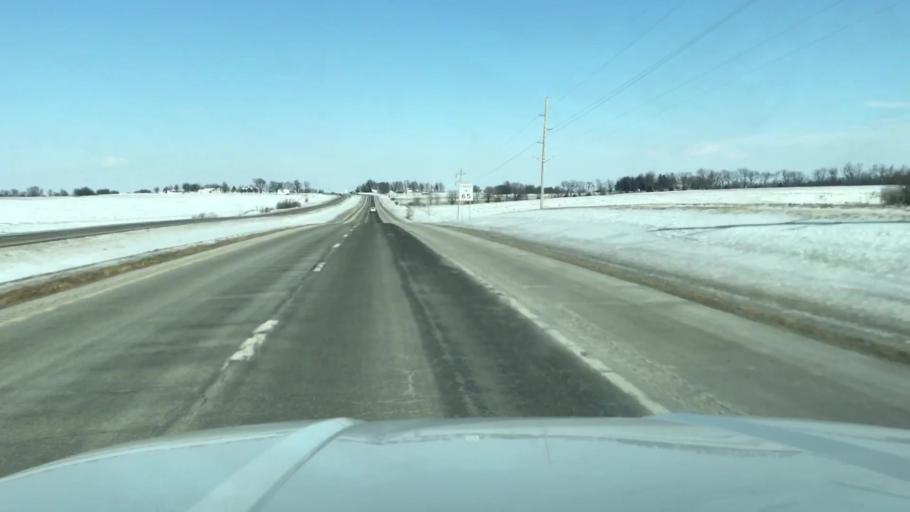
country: US
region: Missouri
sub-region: Nodaway County
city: Maryville
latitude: 40.2604
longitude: -94.8667
